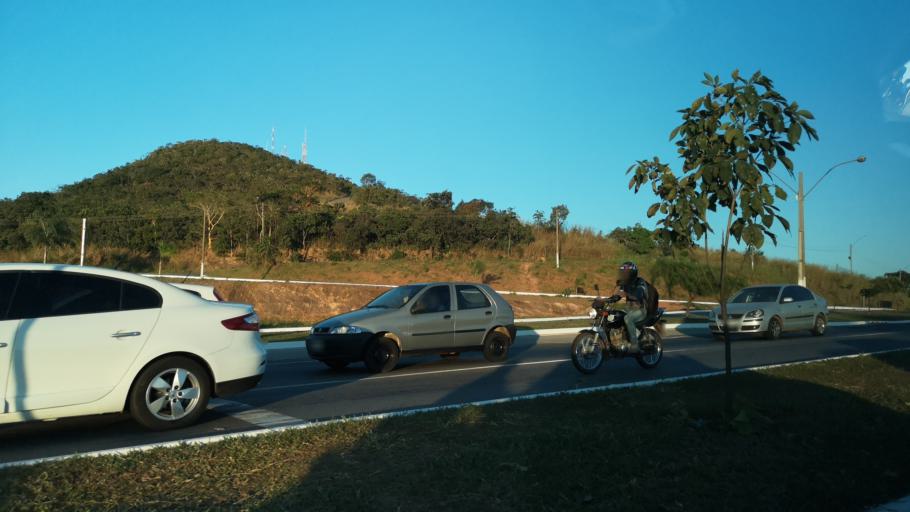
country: BR
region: Goias
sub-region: Senador Canedo
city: Senador Canedo
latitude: -16.6811
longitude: -49.1187
